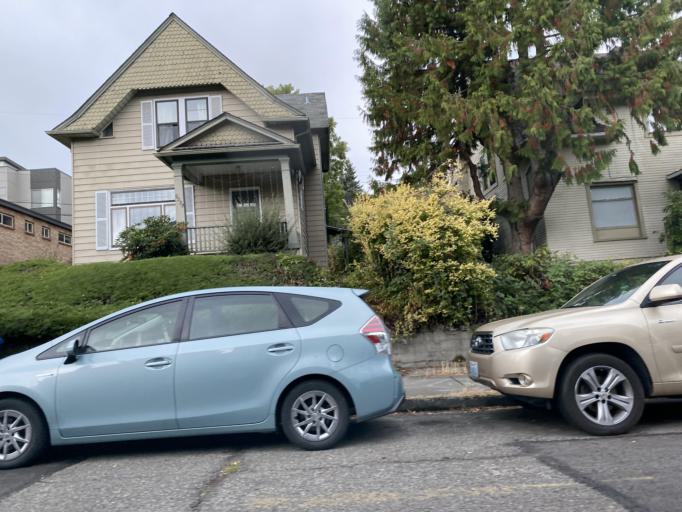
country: US
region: Washington
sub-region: King County
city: Seattle
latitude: 47.6676
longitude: -122.3143
